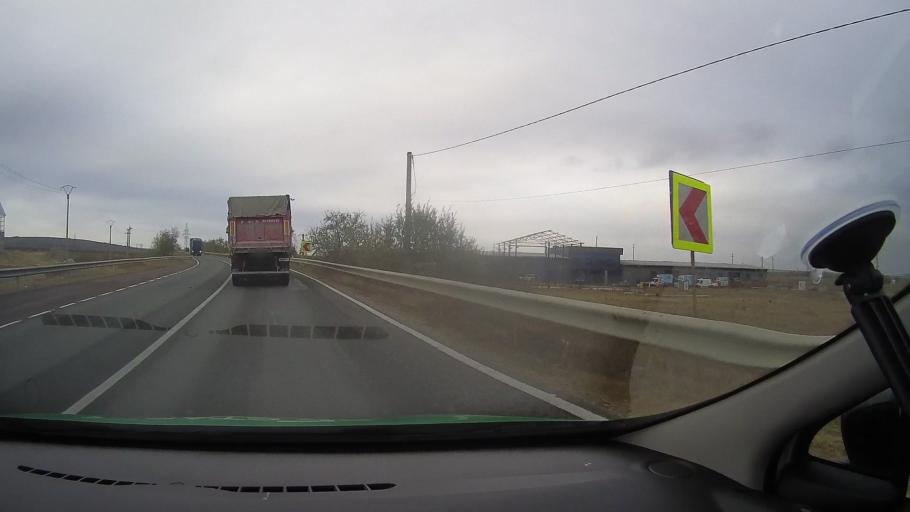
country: RO
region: Constanta
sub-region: Comuna Poarta Alba
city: Poarta Alba
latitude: 44.2136
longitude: 28.3936
